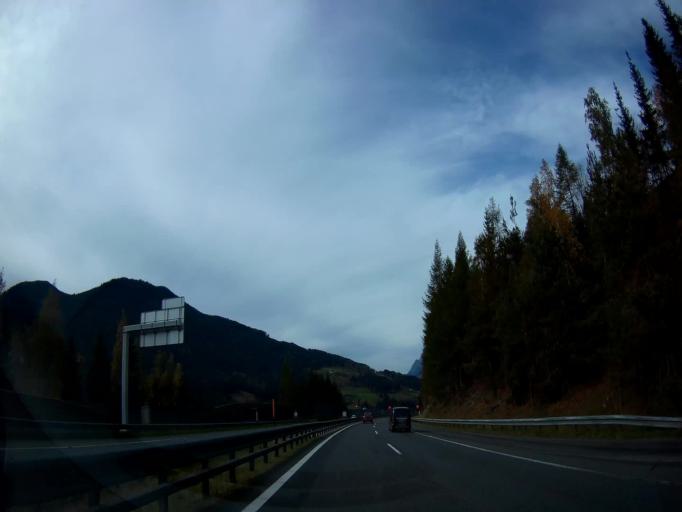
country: AT
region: Salzburg
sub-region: Politischer Bezirk Sankt Johann im Pongau
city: Huttau
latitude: 47.4189
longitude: 13.3180
